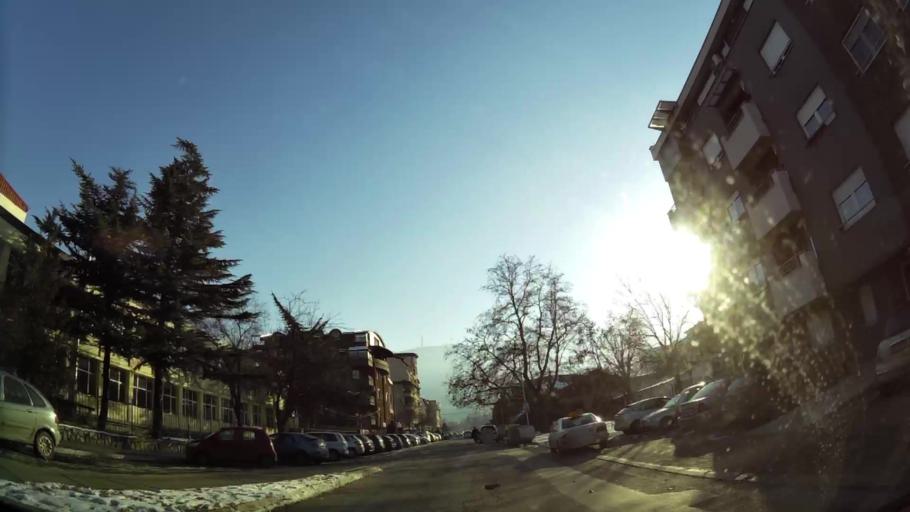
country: MK
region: Karpos
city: Skopje
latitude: 42.0002
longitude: 21.4007
